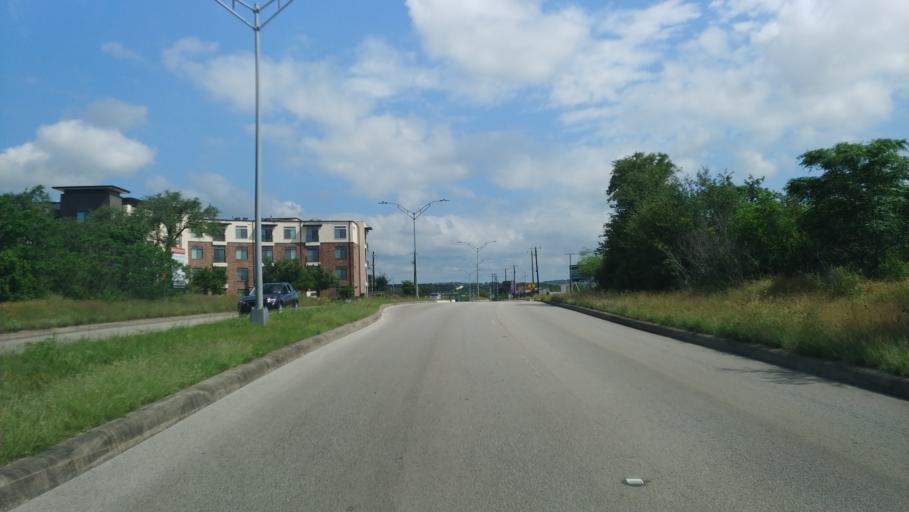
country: US
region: Texas
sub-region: Bexar County
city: Shavano Park
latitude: 29.5879
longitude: -98.5889
